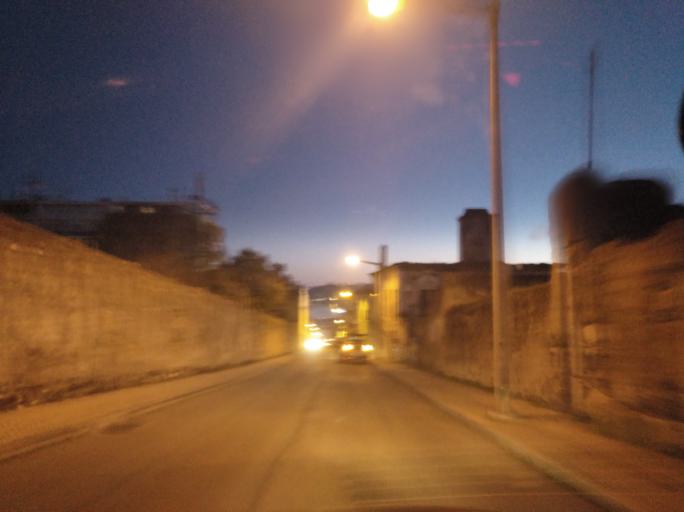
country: PT
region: Lisbon
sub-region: Oeiras
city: Alges
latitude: 38.7060
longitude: -9.1963
